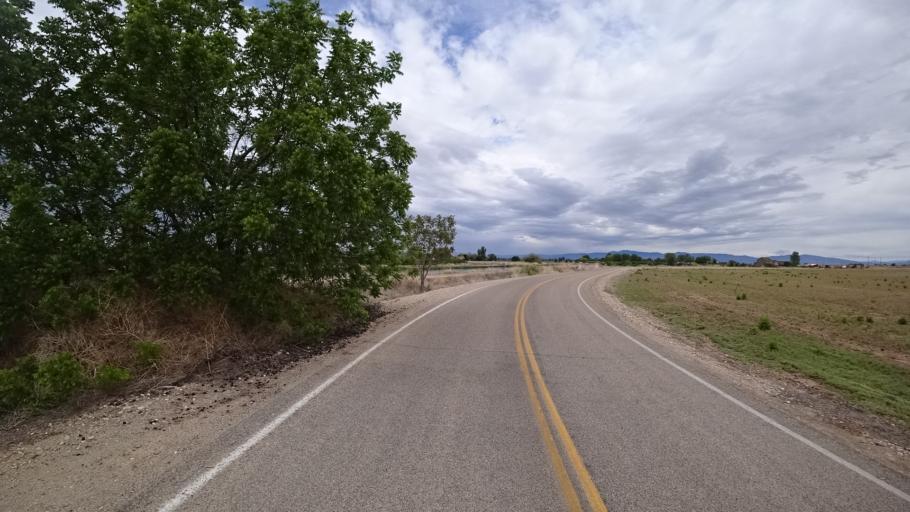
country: US
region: Idaho
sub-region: Ada County
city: Kuna
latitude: 43.4690
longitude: -116.4434
